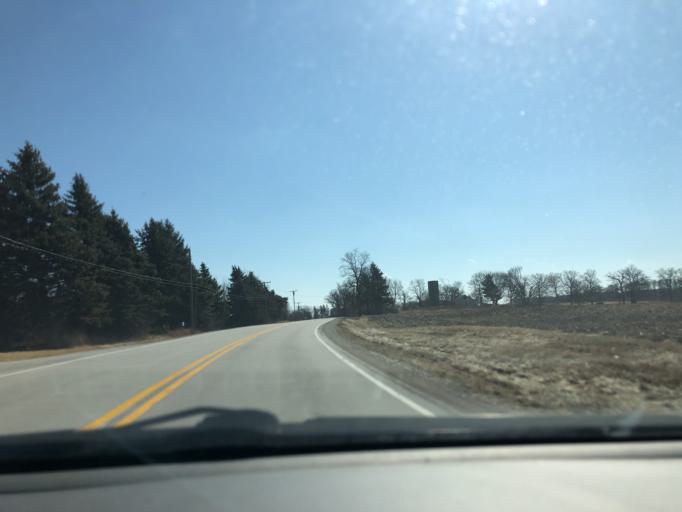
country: US
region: Illinois
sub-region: Kane County
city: Hampshire
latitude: 42.1054
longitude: -88.4876
